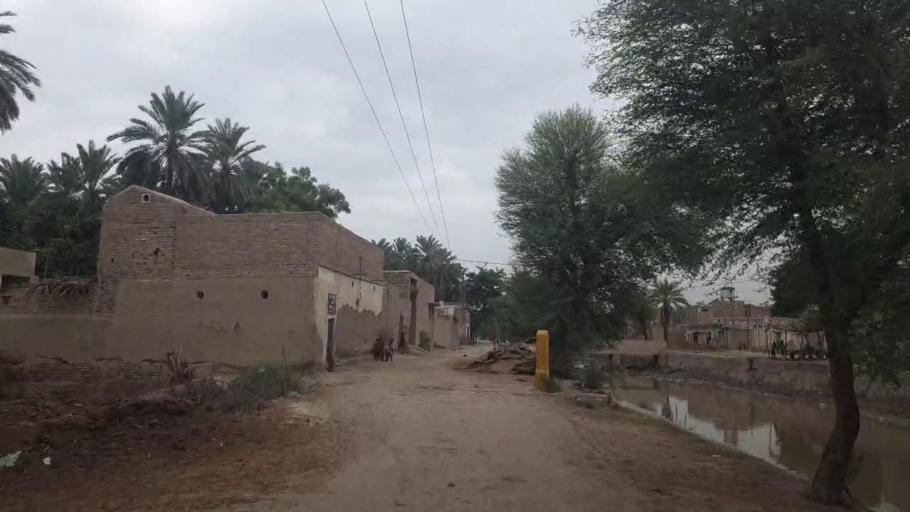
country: PK
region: Sindh
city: Khairpur
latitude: 27.6328
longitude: 68.7776
